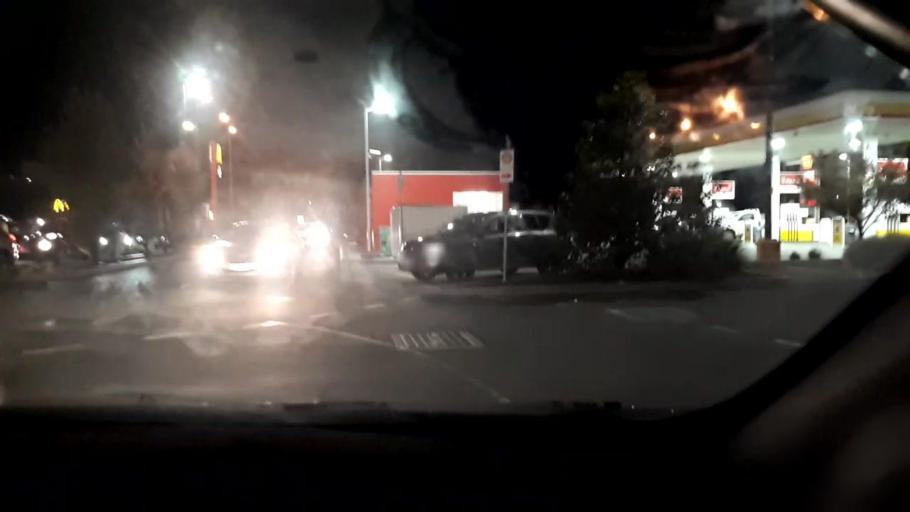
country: AU
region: Victoria
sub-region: Casey
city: Cranbourne East
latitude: -38.1188
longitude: 145.3210
